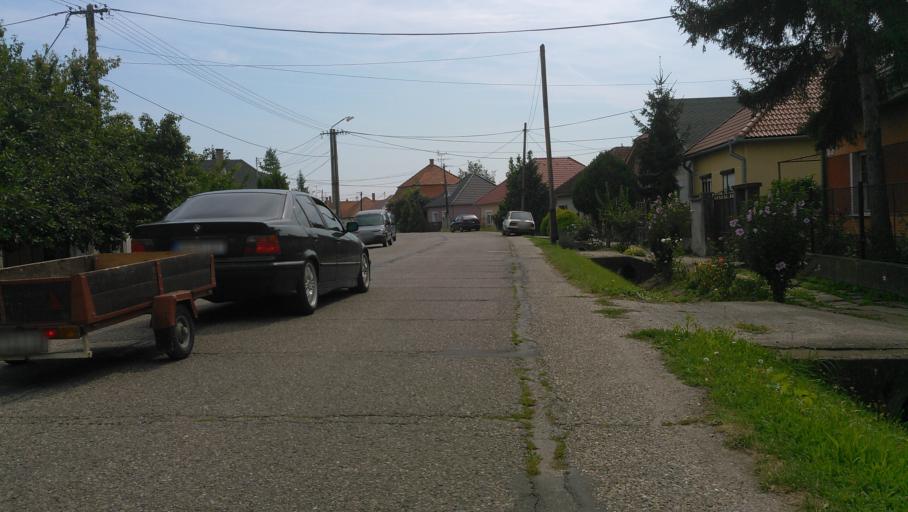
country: SK
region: Nitriansky
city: Kolarovo
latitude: 47.9077
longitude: 18.0002
